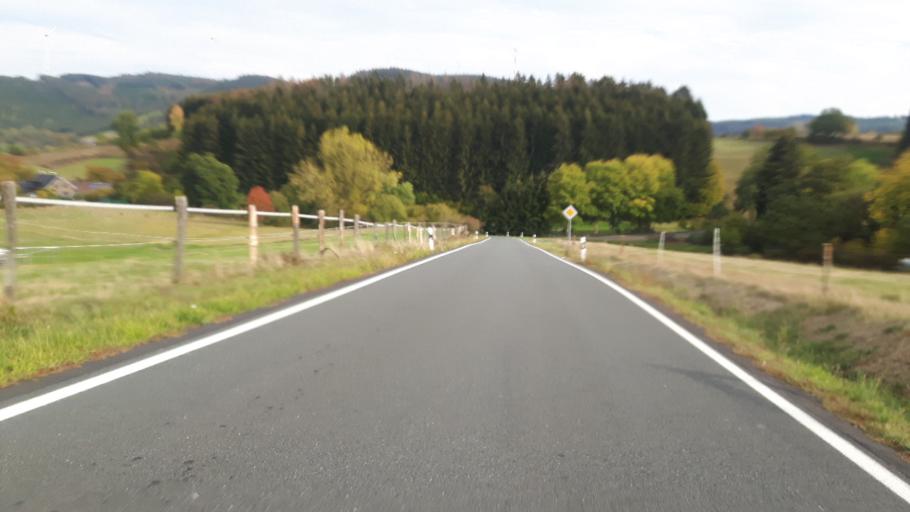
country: DE
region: North Rhine-Westphalia
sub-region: Regierungsbezirk Arnsberg
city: Bad Laasphe
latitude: 50.9129
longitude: 8.3381
